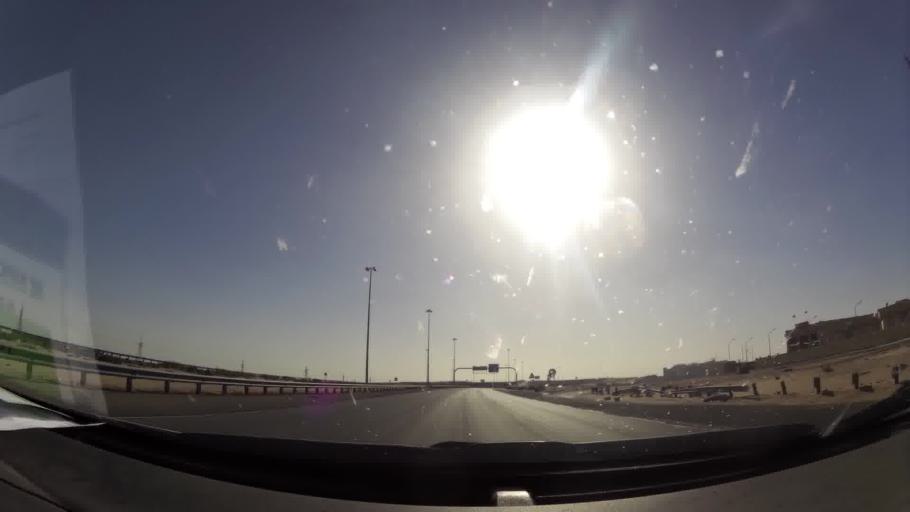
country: KW
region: Al Asimah
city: Kuwait City
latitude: 29.5788
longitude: 47.9037
